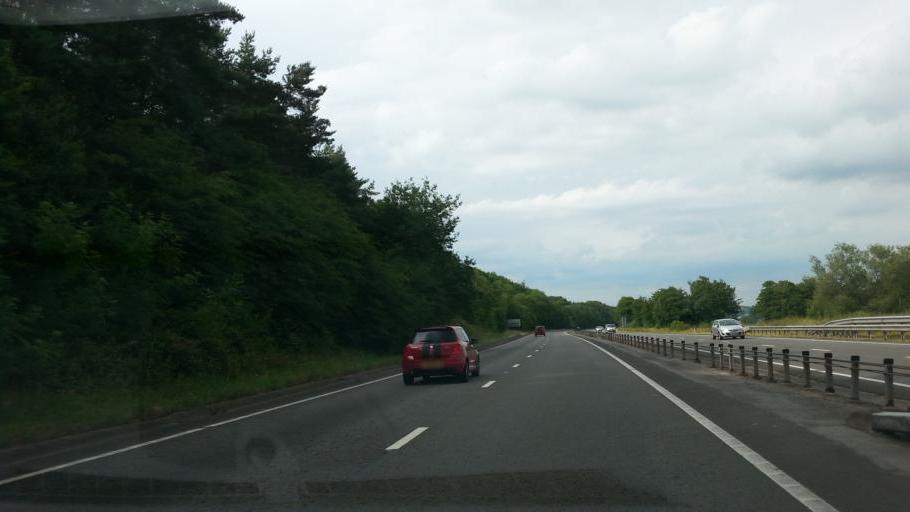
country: GB
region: Wales
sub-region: Monmouthshire
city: Llangwm
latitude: 51.7152
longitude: -2.8618
